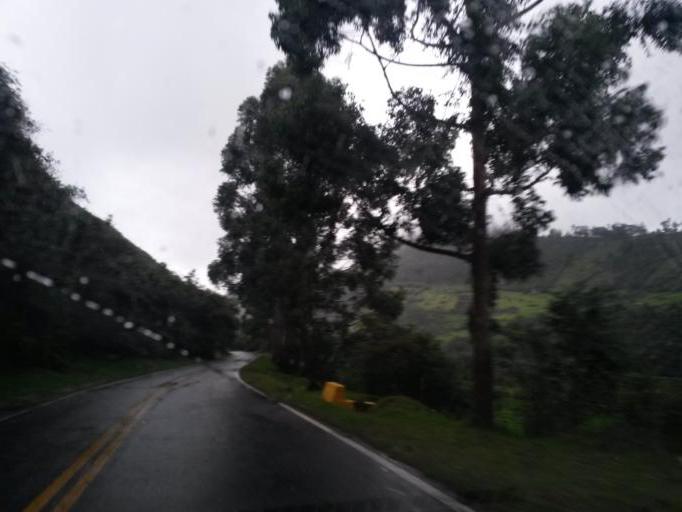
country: CO
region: Cauca
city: Popayan
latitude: 2.3662
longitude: -76.4935
